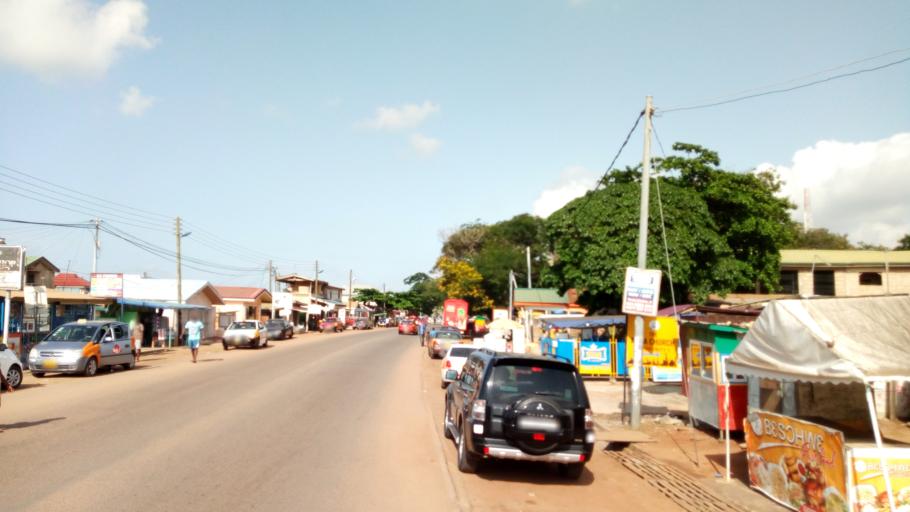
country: GH
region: Greater Accra
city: Tema
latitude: 5.6431
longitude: -0.0028
